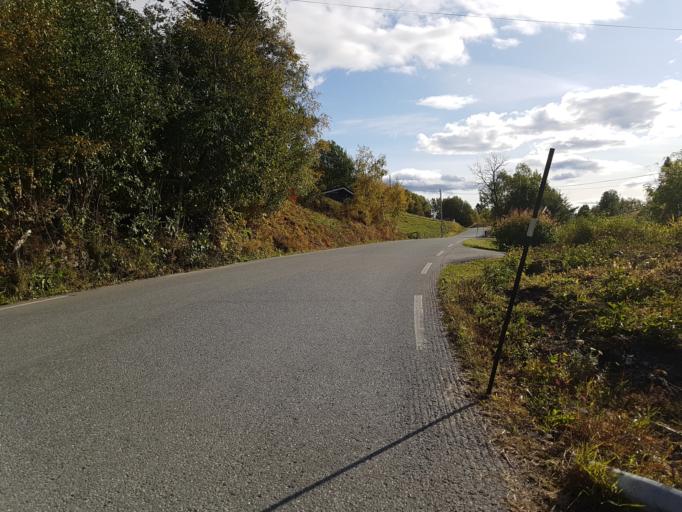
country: NO
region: Sor-Trondelag
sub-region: Malvik
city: Malvik
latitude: 63.3860
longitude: 10.5851
